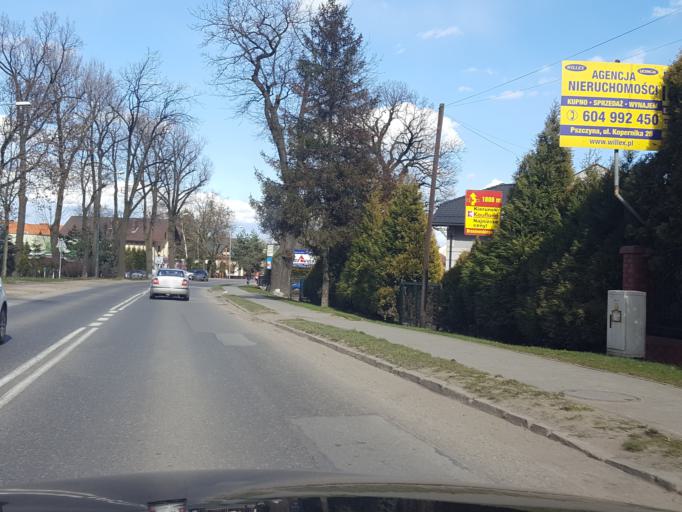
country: PL
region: Silesian Voivodeship
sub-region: Powiat pszczynski
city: Pszczyna
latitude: 49.9701
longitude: 18.9321
